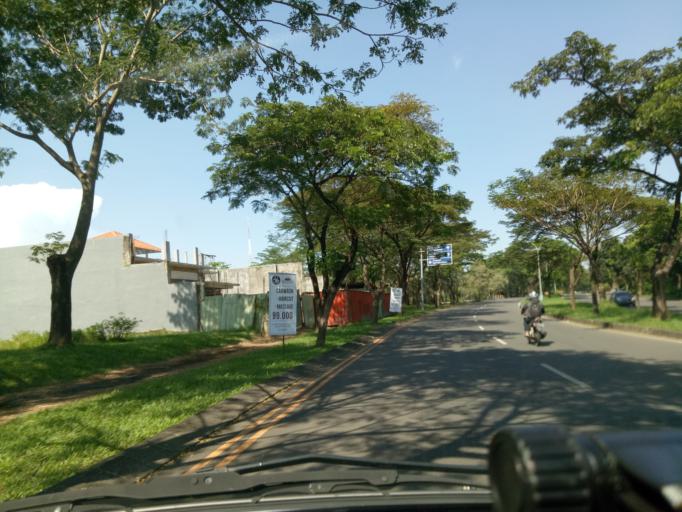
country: ID
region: East Java
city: Driyorejo
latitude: -7.2816
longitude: 112.6413
